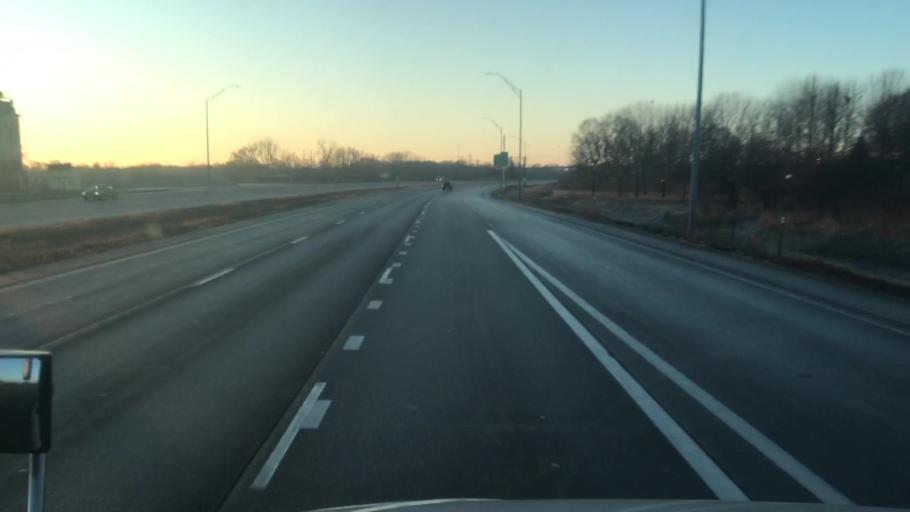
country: US
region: Iowa
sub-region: Black Hawk County
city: Evansdale
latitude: 42.4656
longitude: -92.3165
